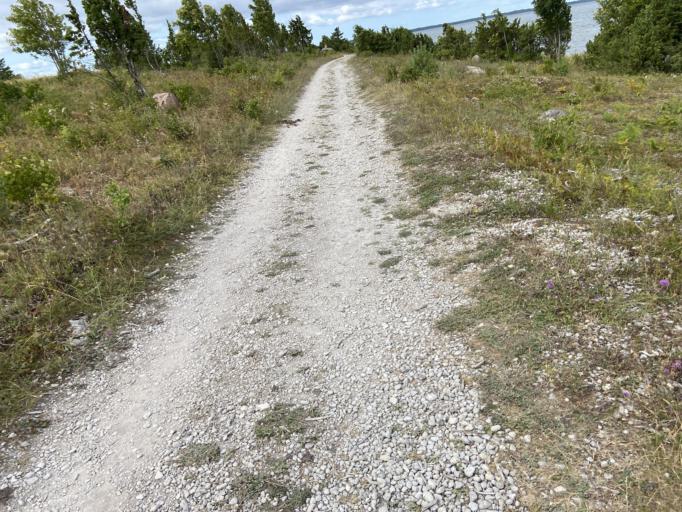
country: EE
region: Hiiumaa
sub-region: Kaerdla linn
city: Kardla
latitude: 58.7622
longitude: 22.8033
